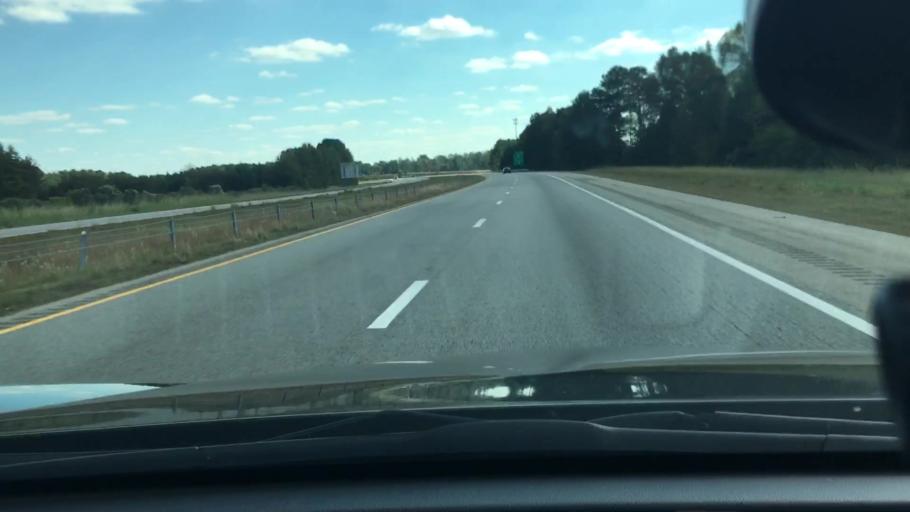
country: US
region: North Carolina
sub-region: Wilson County
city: Lucama
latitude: 35.7178
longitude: -78.0049
